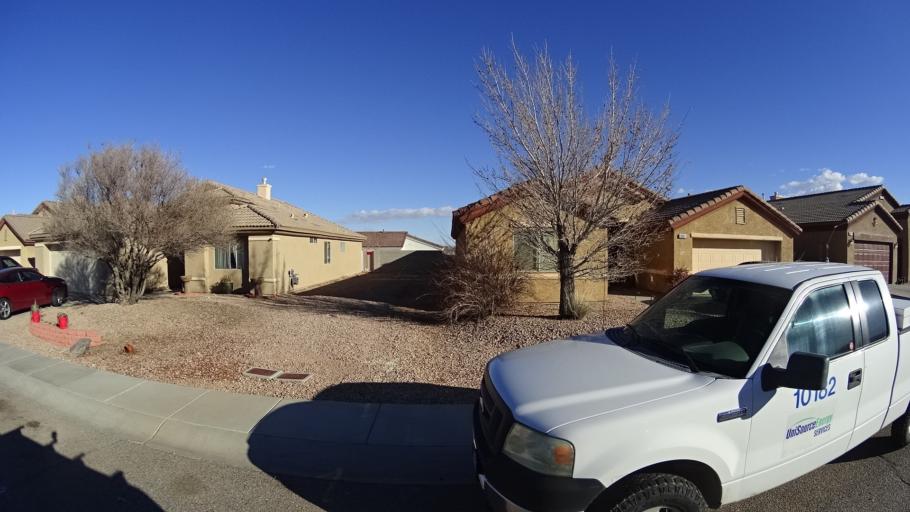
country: US
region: Arizona
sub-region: Mohave County
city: New Kingman-Butler
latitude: 35.2253
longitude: -113.9835
